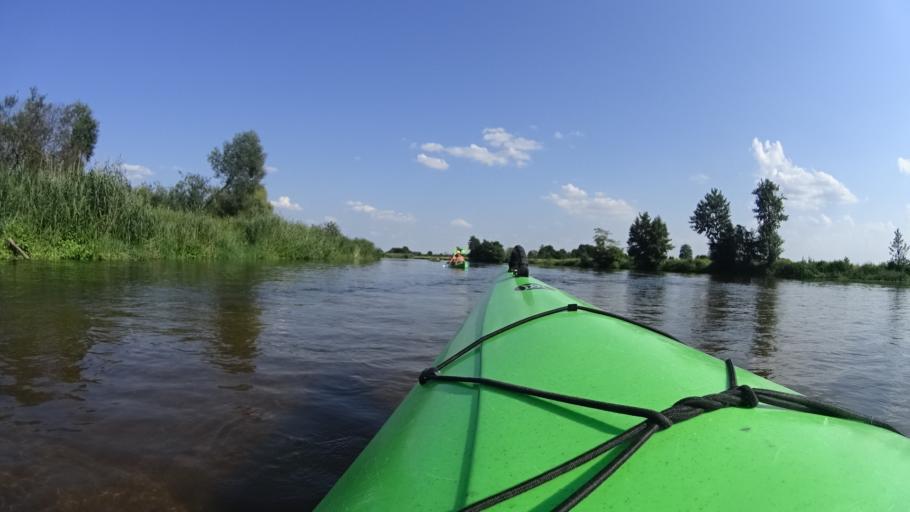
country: PL
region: Masovian Voivodeship
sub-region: Powiat bialobrzeski
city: Bialobrzegi
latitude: 51.6625
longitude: 20.9274
